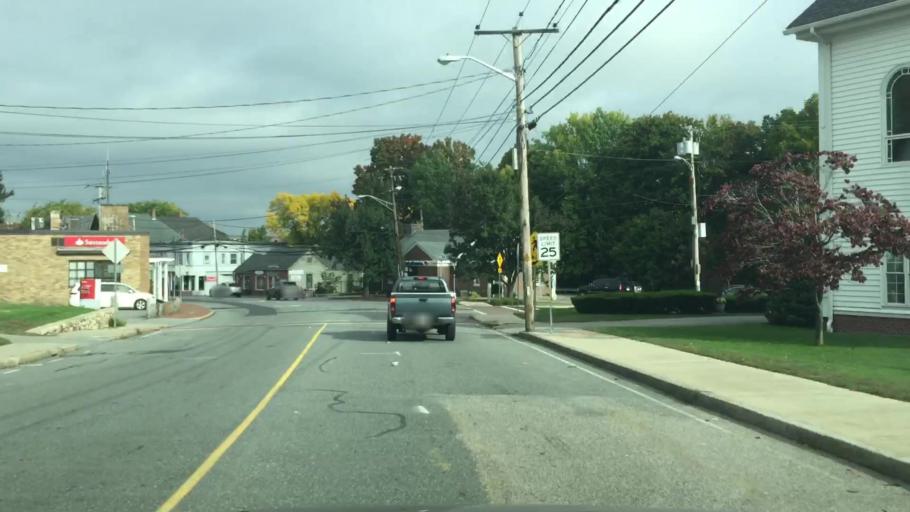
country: US
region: Massachusetts
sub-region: Essex County
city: North Andover
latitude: 42.7014
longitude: -71.1297
